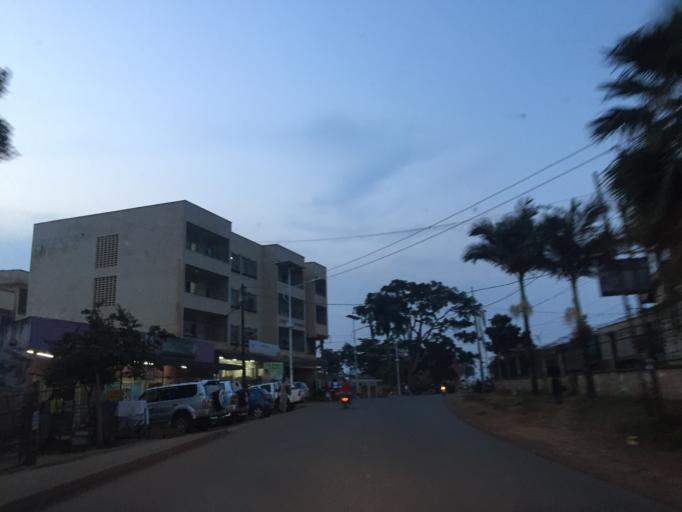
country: UG
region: Central Region
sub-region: Kampala District
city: Kampala
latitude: 0.3022
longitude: 32.6017
